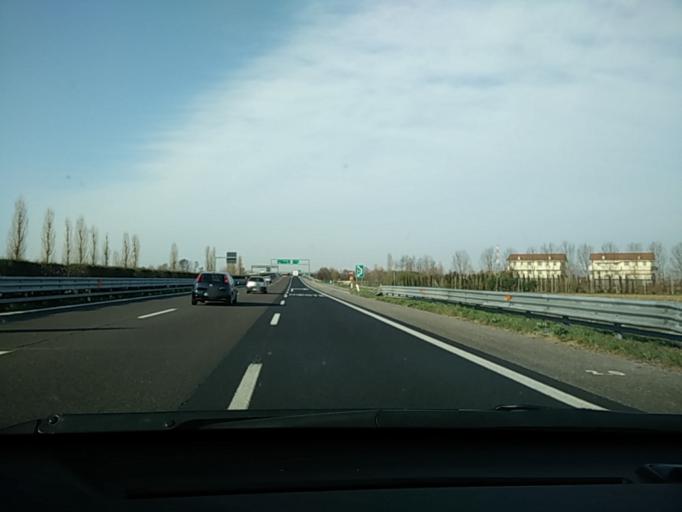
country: IT
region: Veneto
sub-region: Provincia di Venezia
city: Marano
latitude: 45.4525
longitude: 12.1044
